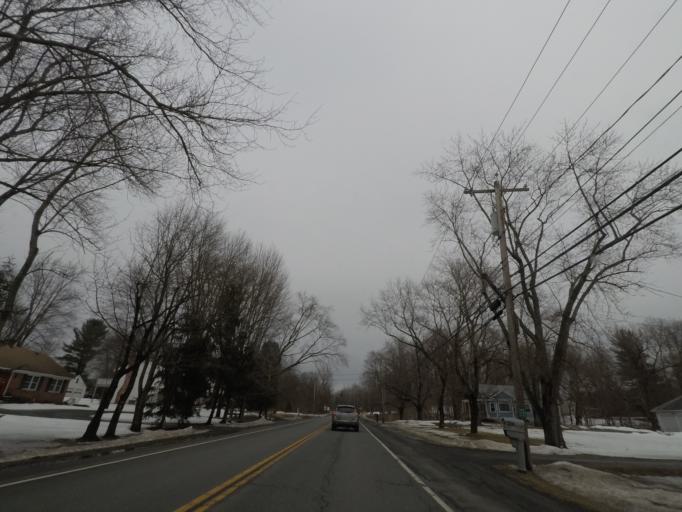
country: US
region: New York
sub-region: Albany County
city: Voorheesville
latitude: 42.7052
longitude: -73.9282
